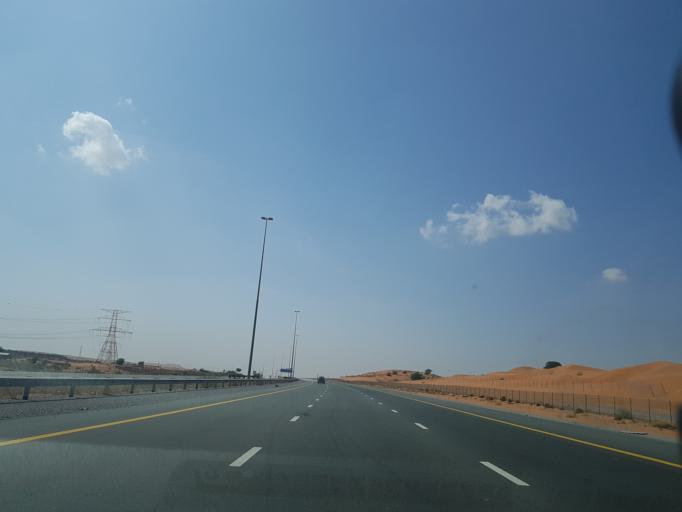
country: AE
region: Ra's al Khaymah
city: Ras al-Khaimah
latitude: 25.6801
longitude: 55.9051
